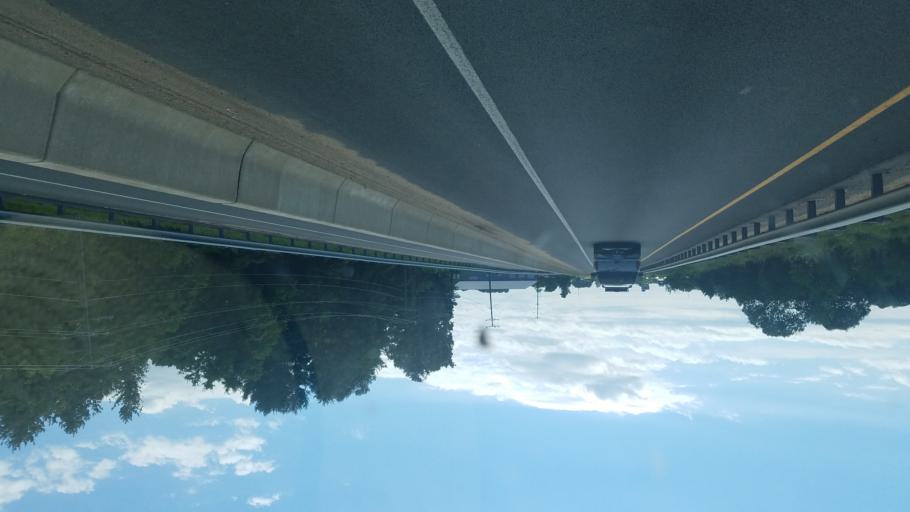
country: US
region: Virginia
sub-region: Fauquier County
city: Bealeton
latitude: 38.6135
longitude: -77.7984
